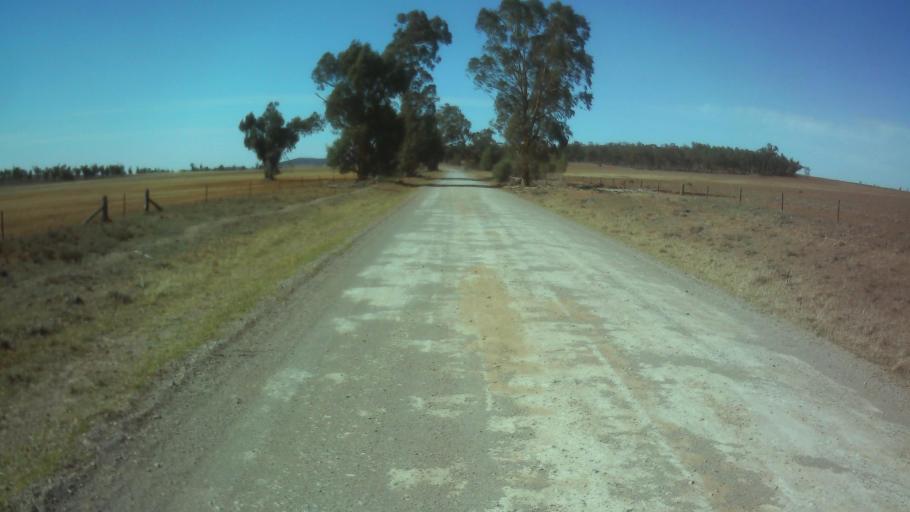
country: AU
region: New South Wales
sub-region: Forbes
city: Forbes
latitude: -33.7184
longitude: 147.7462
